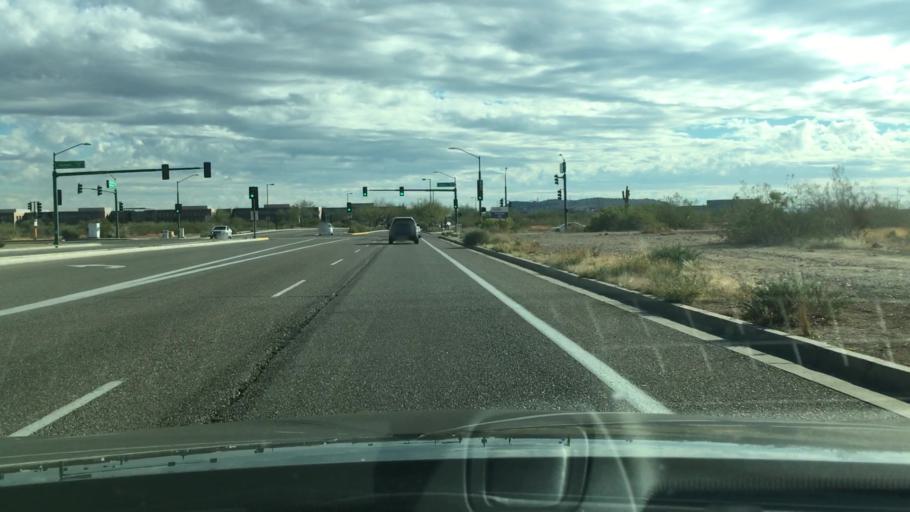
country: US
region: Arizona
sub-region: Maricopa County
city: Anthem
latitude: 33.7266
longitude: -112.1138
